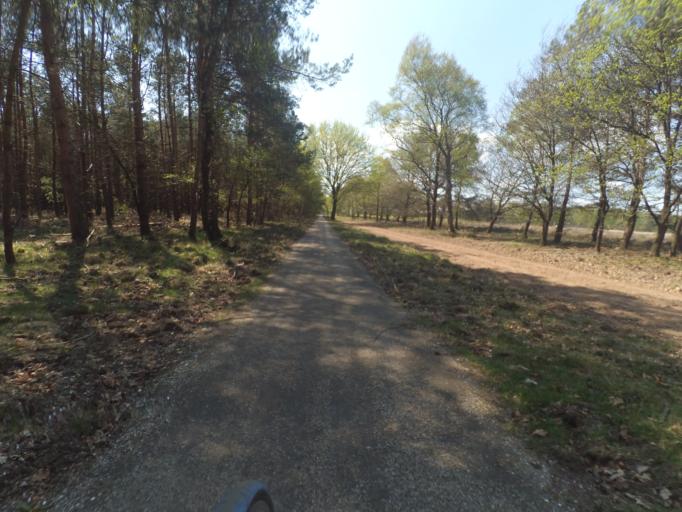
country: NL
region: Gelderland
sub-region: Gemeente Apeldoorn
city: Uddel
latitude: 52.3067
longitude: 5.7645
